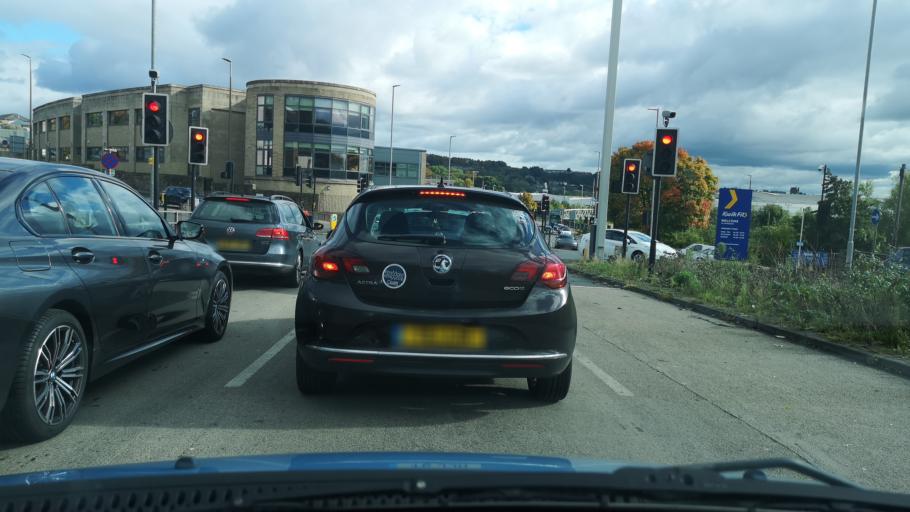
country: GB
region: England
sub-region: Kirklees
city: Dewsbury
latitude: 53.6896
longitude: -1.6364
